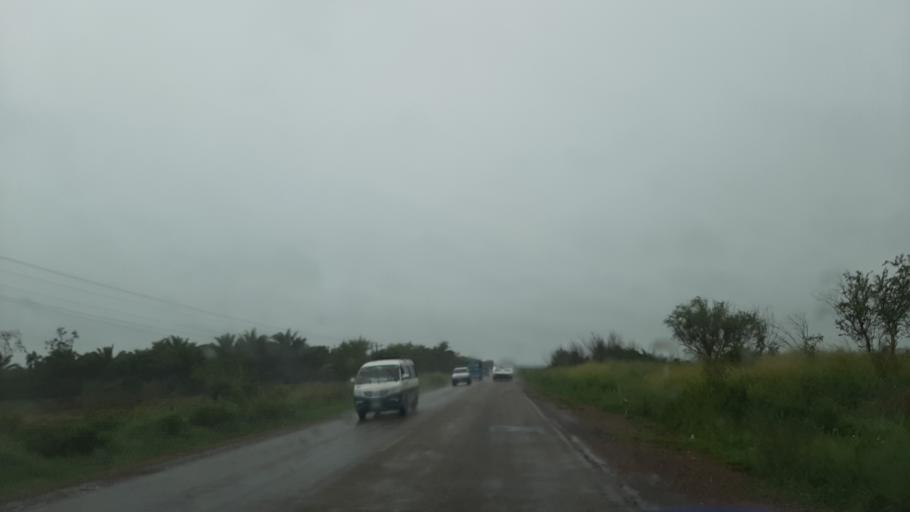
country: BO
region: Santa Cruz
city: Okinawa Numero Uno
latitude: -16.8022
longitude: -62.5976
